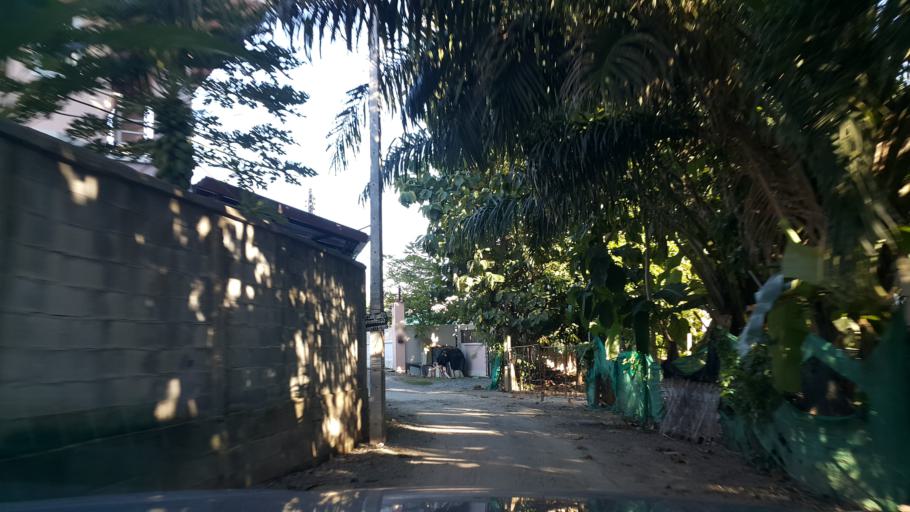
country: TH
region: Chiang Mai
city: Saraphi
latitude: 18.7500
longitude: 99.0521
